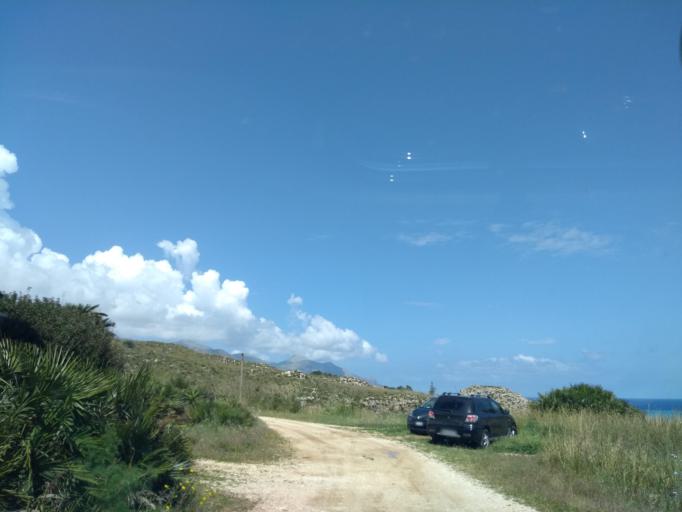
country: IT
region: Sicily
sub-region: Trapani
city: Castellammare del Golfo
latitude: 38.0507
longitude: 12.8524
